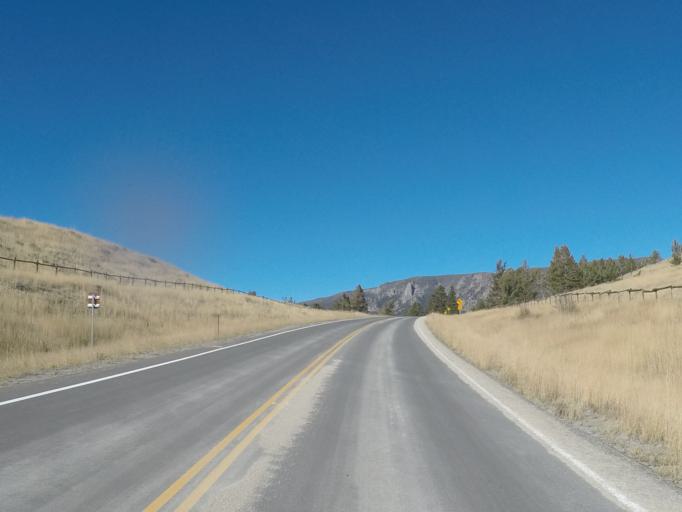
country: US
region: Montana
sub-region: Carbon County
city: Red Lodge
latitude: 44.8005
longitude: -109.4463
